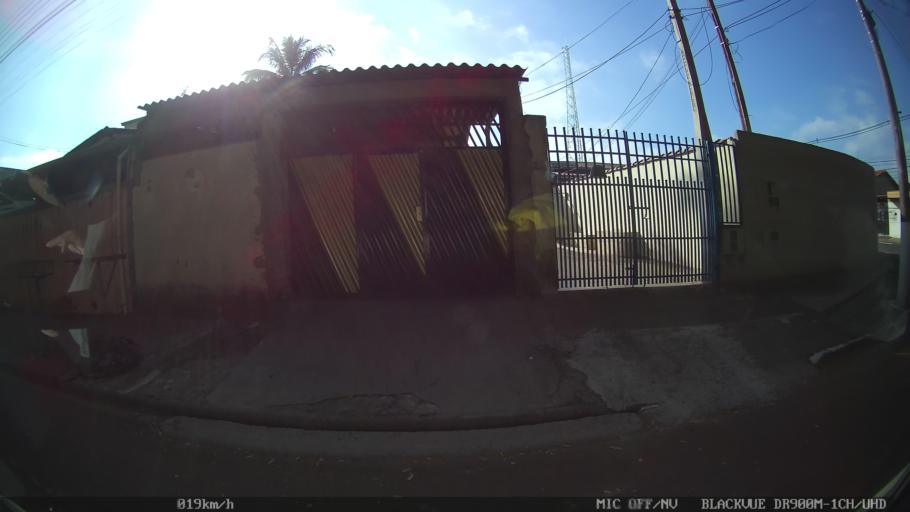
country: BR
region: Sao Paulo
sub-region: Hortolandia
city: Hortolandia
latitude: -22.9077
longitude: -47.1796
